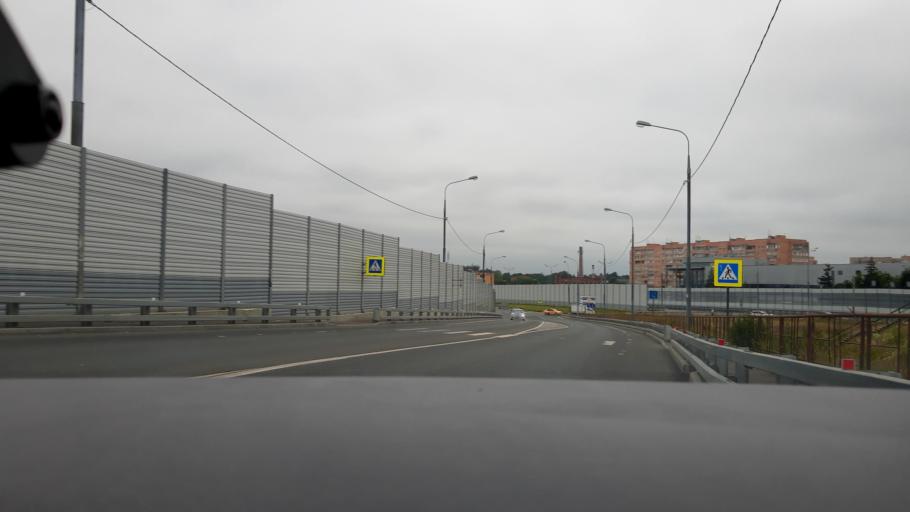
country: RU
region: Moskovskaya
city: Aprelevka
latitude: 55.5381
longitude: 37.0822
